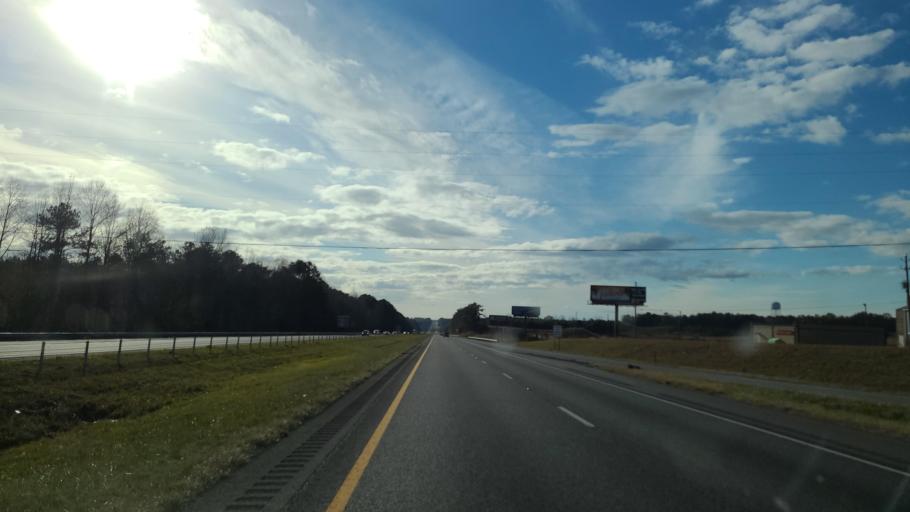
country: US
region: Alabama
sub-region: Cleburne County
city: Heflin
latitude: 33.6447
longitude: -85.5063
